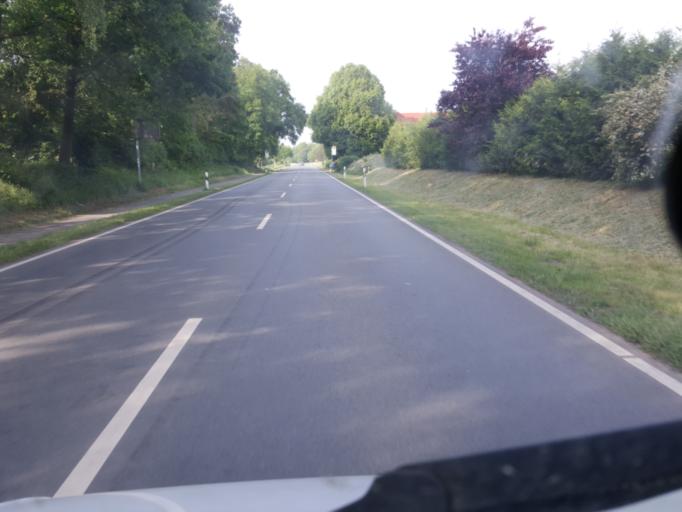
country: DE
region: Lower Saxony
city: Liebenau
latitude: 52.5924
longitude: 9.0954
